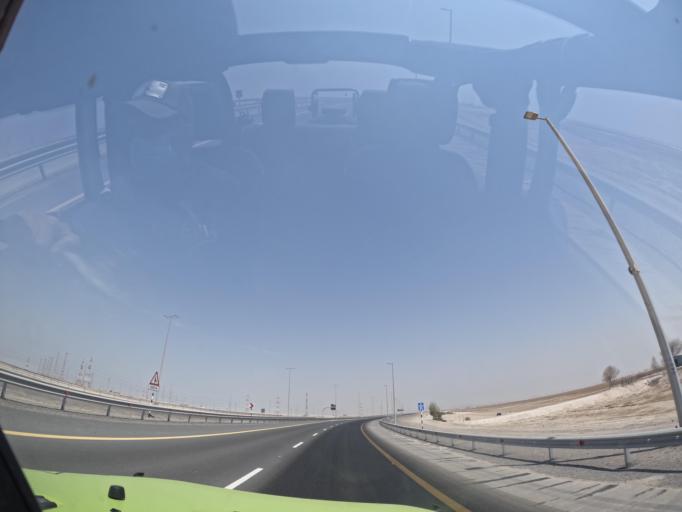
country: AE
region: Abu Dhabi
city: Abu Dhabi
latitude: 24.1501
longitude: 54.2434
